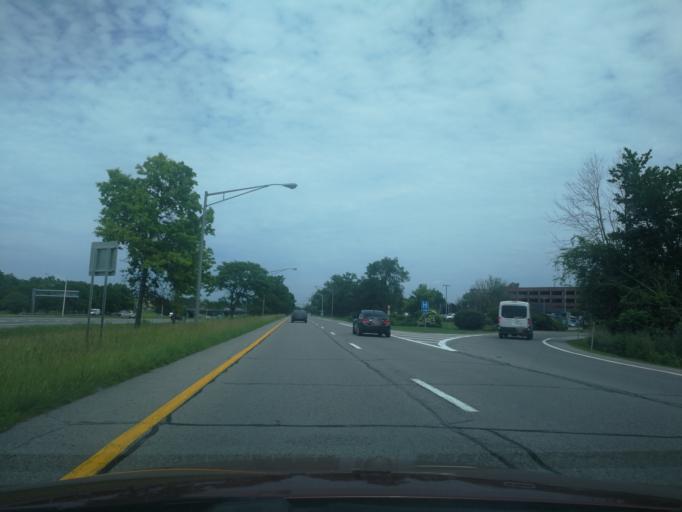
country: US
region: New York
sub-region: Monroe County
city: Irondequoit
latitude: 43.1937
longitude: -77.5889
